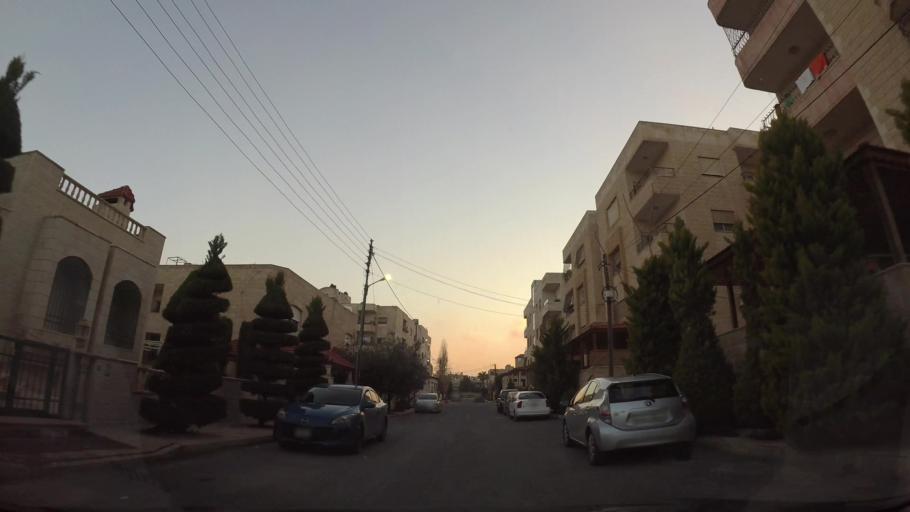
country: JO
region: Amman
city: Amman
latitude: 31.9957
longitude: 35.9513
